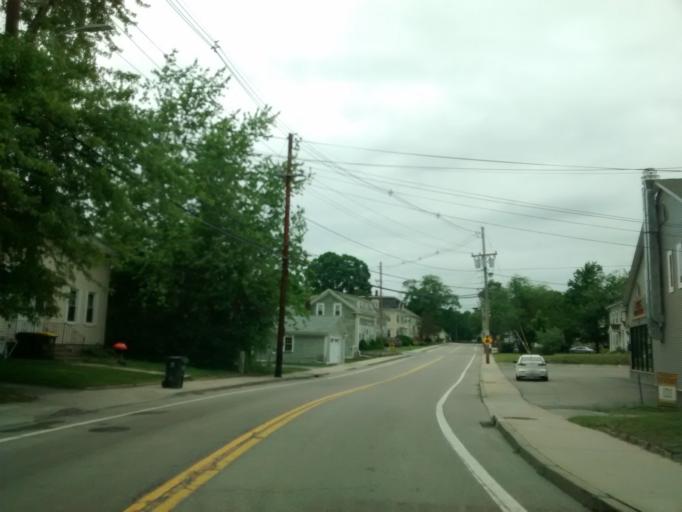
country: US
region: Rhode Island
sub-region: Providence County
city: Harrisville
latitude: 41.9635
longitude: -71.6750
